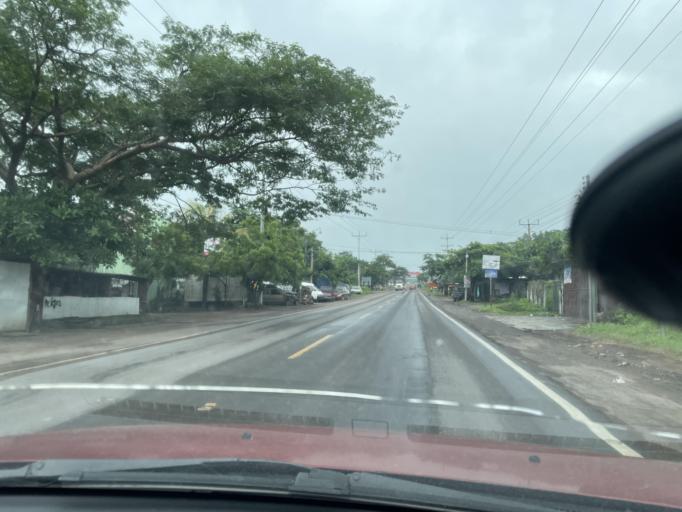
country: SV
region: San Miguel
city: San Miguel
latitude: 13.5085
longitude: -88.1533
